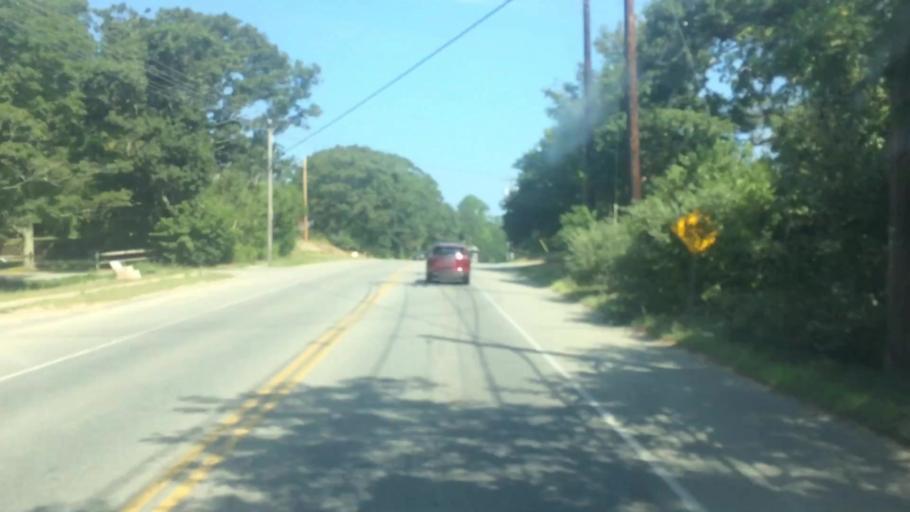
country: US
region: Massachusetts
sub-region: Dukes County
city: Vineyard Haven
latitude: 41.4439
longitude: -70.6091
